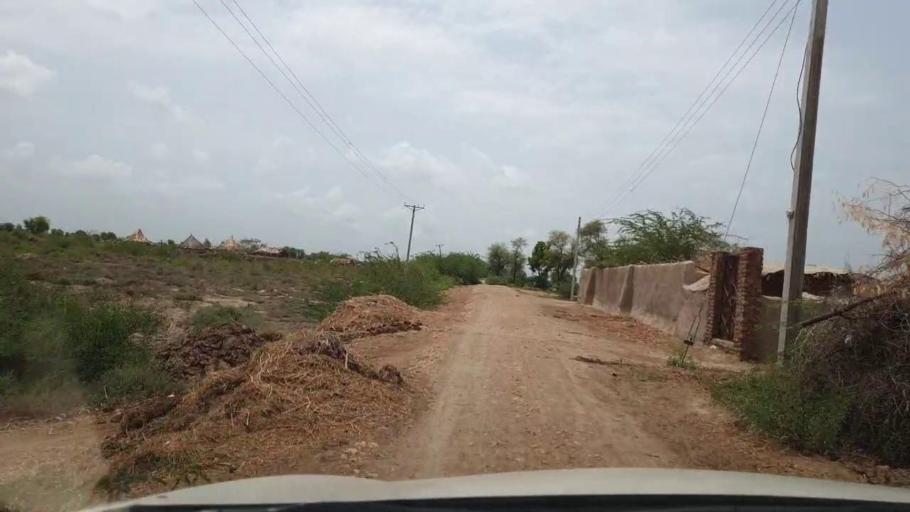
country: PK
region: Sindh
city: Chambar
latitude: 25.2113
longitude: 68.7616
